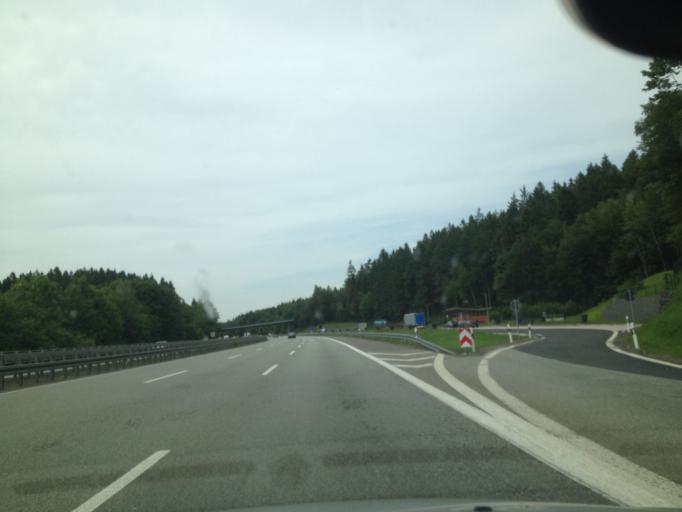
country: DE
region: North Rhine-Westphalia
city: Meinerzhagen
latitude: 51.1211
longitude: 7.6674
